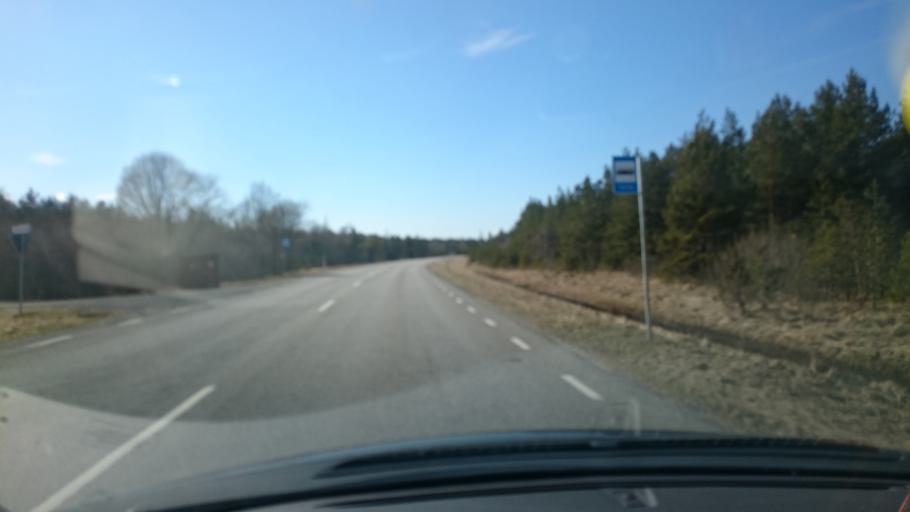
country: EE
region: Laeaene
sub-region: Lihula vald
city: Lihula
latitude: 58.6113
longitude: 23.9271
